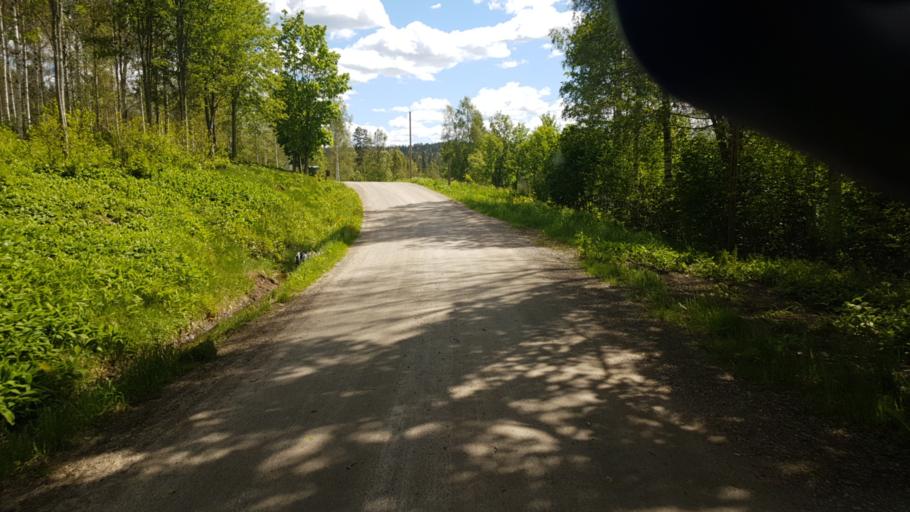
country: SE
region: Vaermland
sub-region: Arvika Kommun
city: Arvika
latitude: 59.7147
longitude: 12.8469
